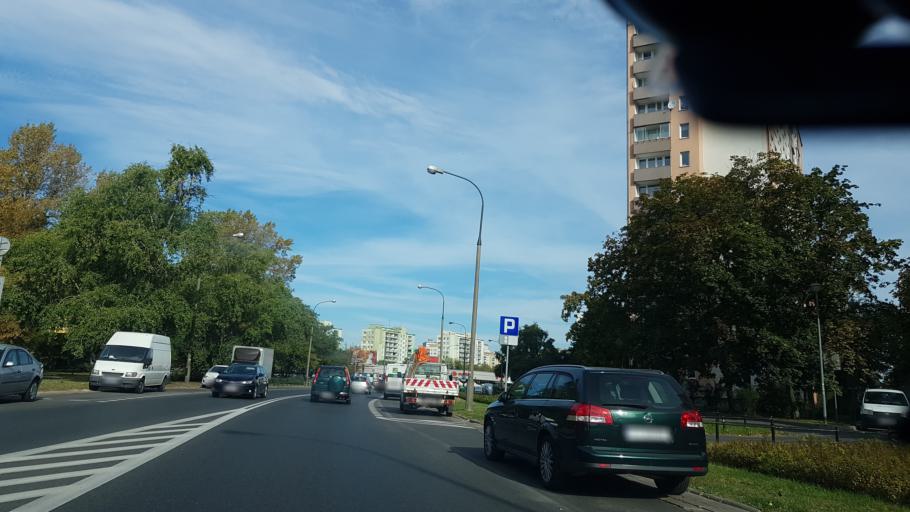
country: PL
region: Masovian Voivodeship
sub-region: Warszawa
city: Bielany
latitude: 52.2736
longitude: 20.9244
